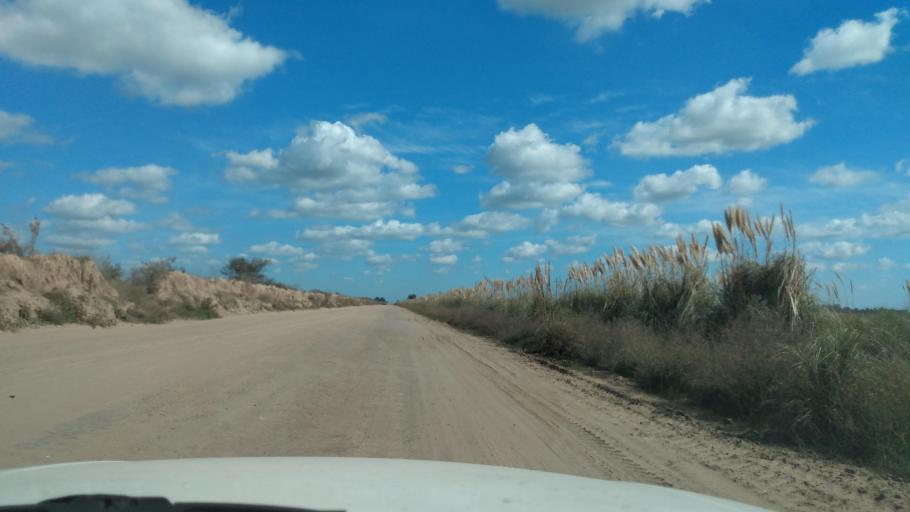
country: AR
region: Buenos Aires
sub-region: Partido de Navarro
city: Navarro
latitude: -35.0028
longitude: -59.3602
